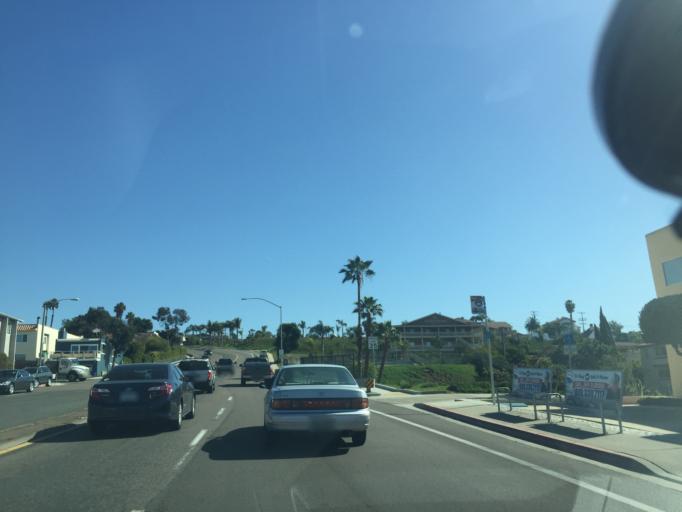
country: US
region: California
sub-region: San Diego County
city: San Diego
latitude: 32.7903
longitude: -117.2030
